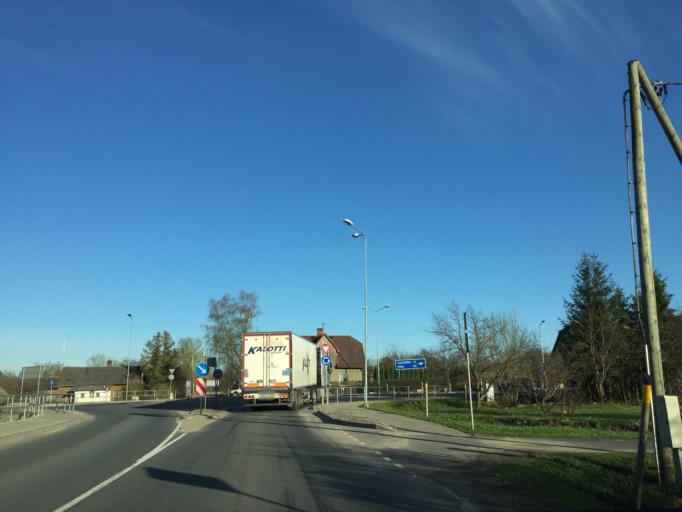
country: LV
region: Valkas Rajons
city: Valka
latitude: 57.7666
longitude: 26.0044
